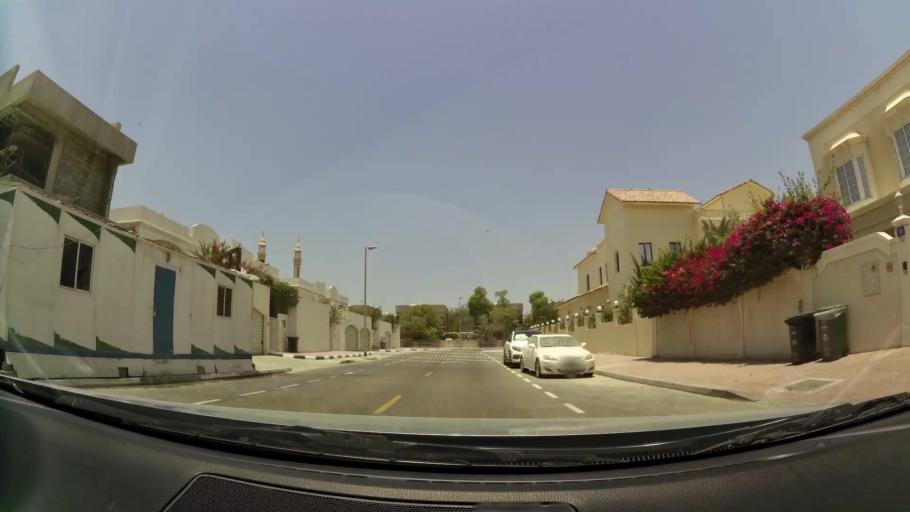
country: AE
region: Dubai
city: Dubai
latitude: 25.1729
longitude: 55.2244
